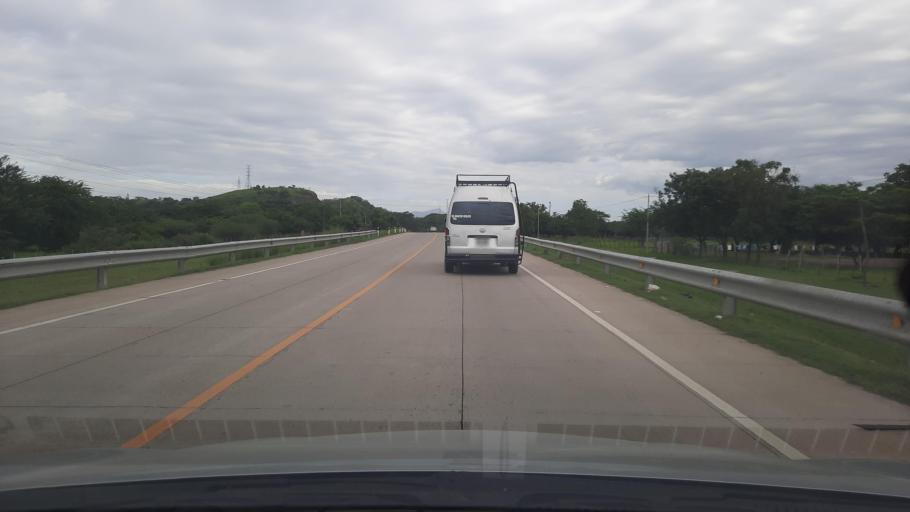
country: NI
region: Chinandega
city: Somotillo
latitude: 12.8753
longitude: -86.8517
